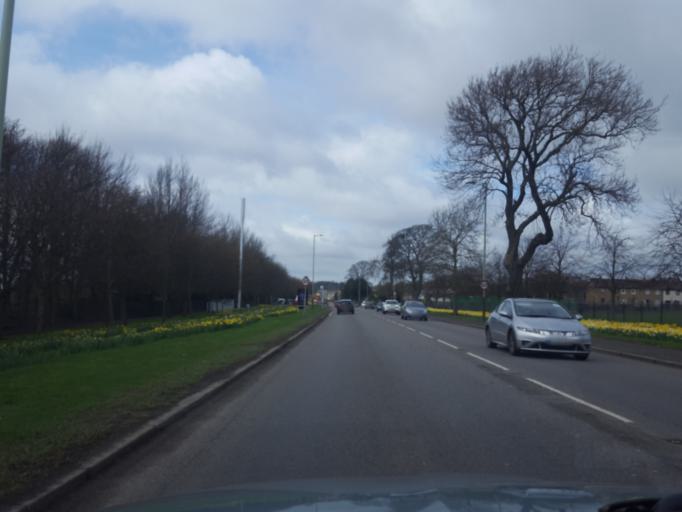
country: GB
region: Scotland
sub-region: Fife
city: Newport-On-Tay
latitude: 56.4745
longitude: -2.9129
